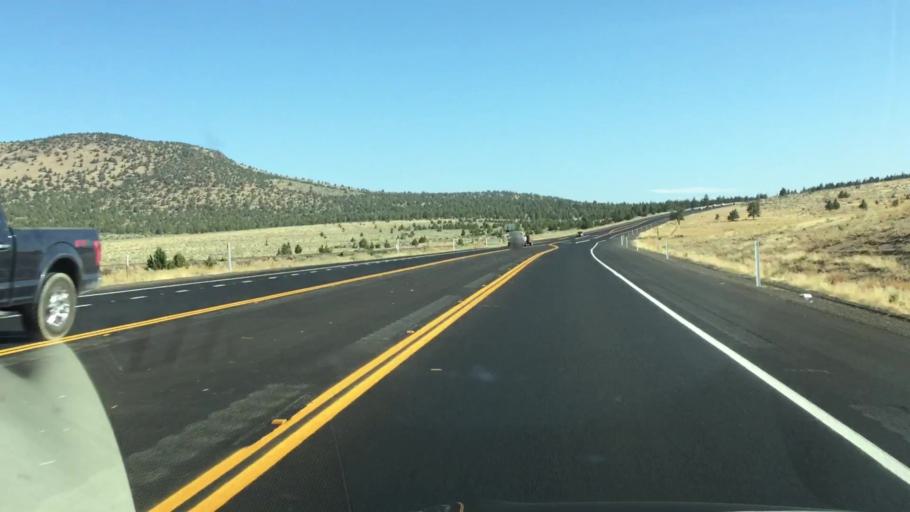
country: US
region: Oregon
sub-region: Jefferson County
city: Culver
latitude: 44.4607
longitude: -121.1996
